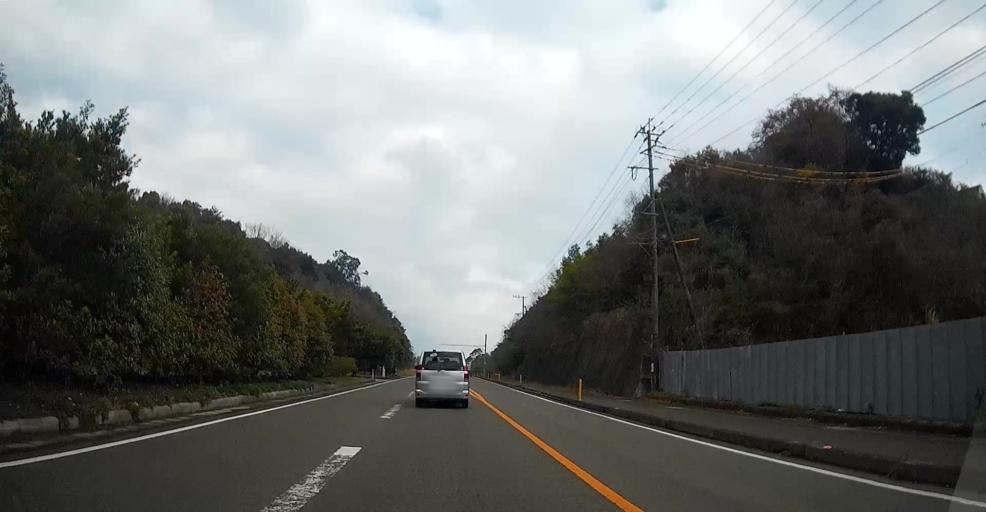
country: JP
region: Kumamoto
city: Yatsushiro
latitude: 32.5570
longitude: 130.4157
